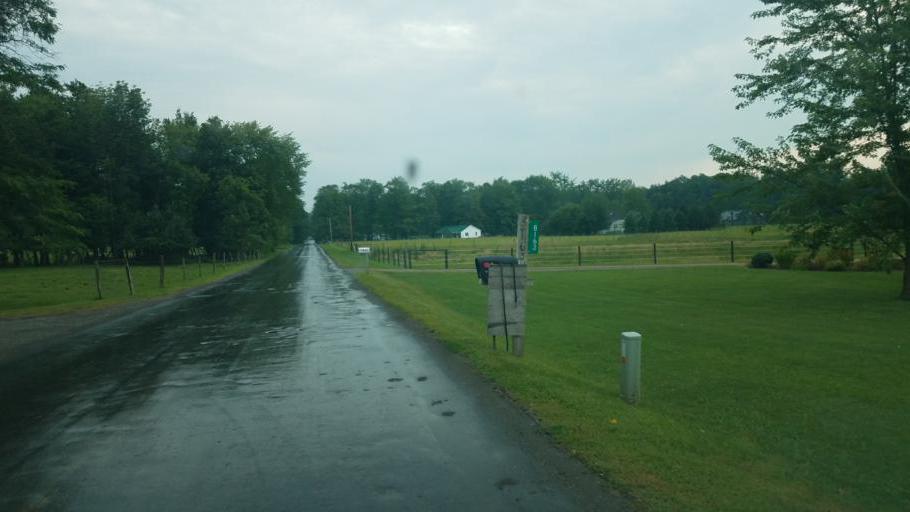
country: US
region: Ohio
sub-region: Geauga County
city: Middlefield
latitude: 41.4432
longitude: -80.9920
